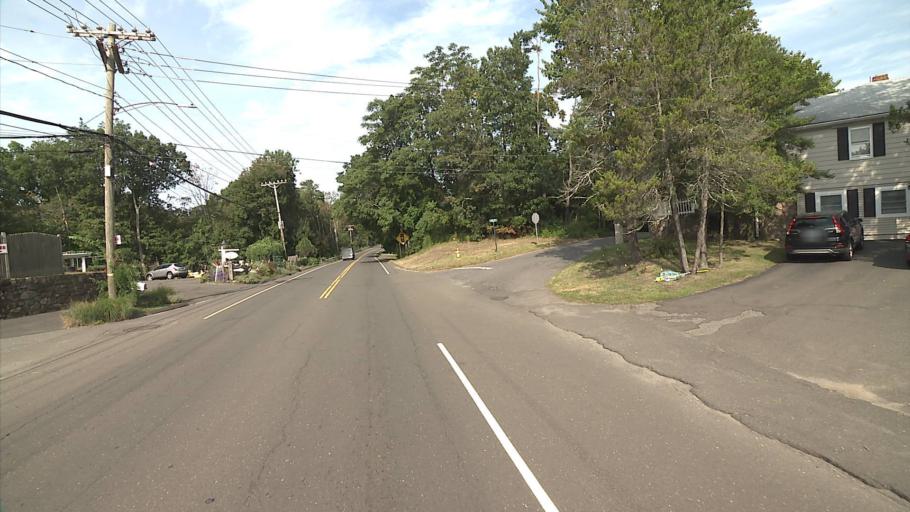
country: US
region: Connecticut
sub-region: Fairfield County
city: New Canaan
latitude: 41.1506
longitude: -73.4870
